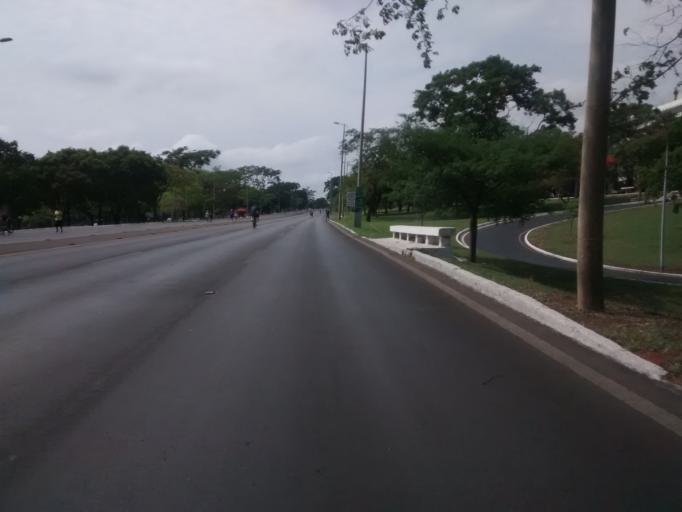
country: BR
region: Federal District
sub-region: Brasilia
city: Brasilia
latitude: -15.7643
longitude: -47.8835
